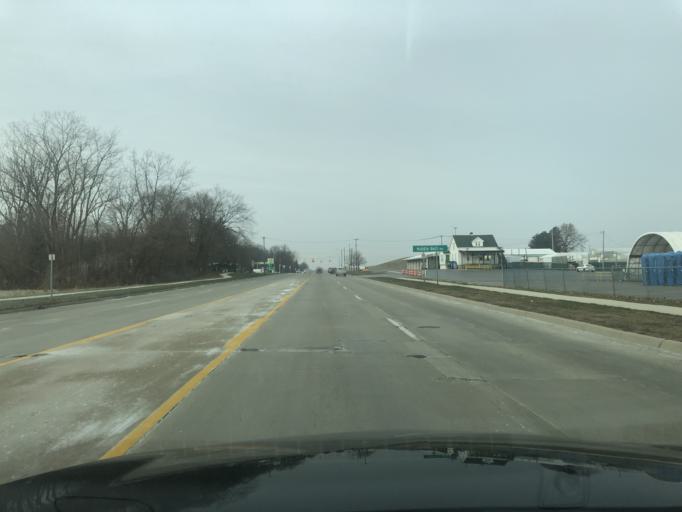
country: US
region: Michigan
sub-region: Wayne County
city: Taylor
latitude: 42.1956
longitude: -83.3228
